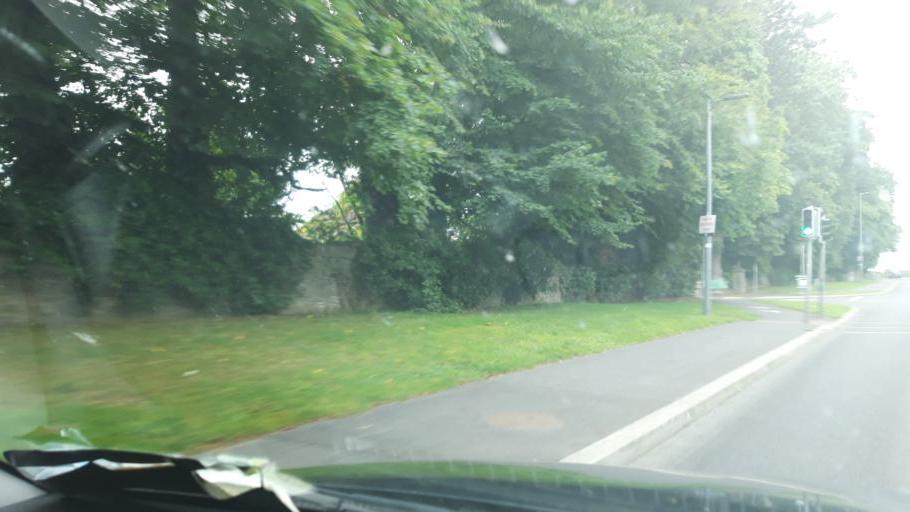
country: IE
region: Leinster
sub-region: Kilkenny
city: Kilkenny
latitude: 52.6389
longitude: -7.2692
